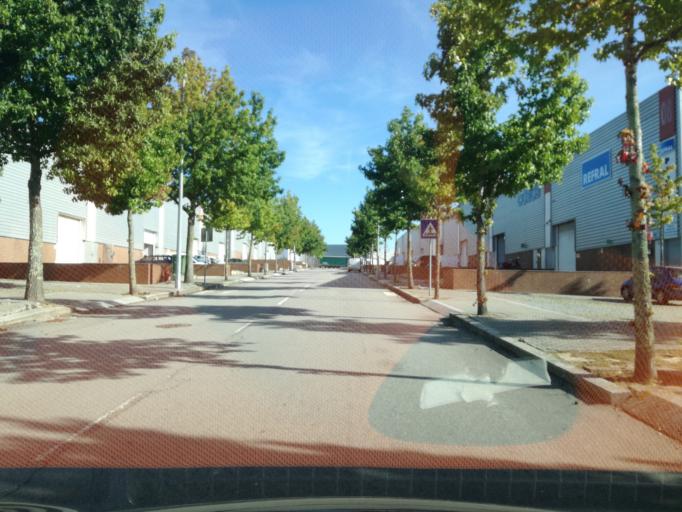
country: PT
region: Porto
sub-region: Maia
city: Anta
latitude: 41.2748
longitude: -8.6048
